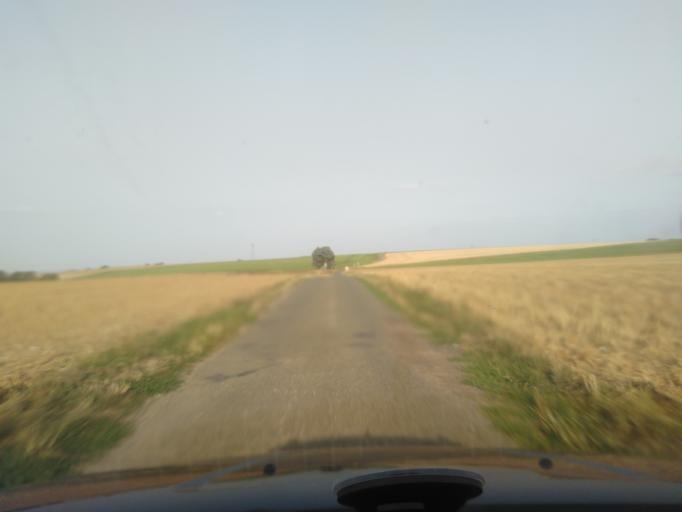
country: FR
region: Champagne-Ardenne
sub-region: Departement de la Marne
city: Fismes
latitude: 49.3508
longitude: 3.6539
